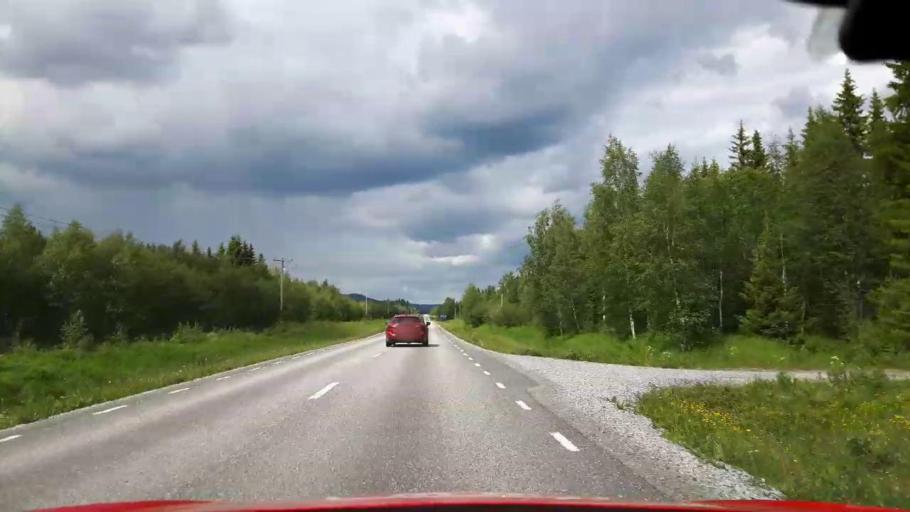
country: SE
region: Jaemtland
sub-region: Krokoms Kommun
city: Krokom
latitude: 63.6552
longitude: 14.3691
